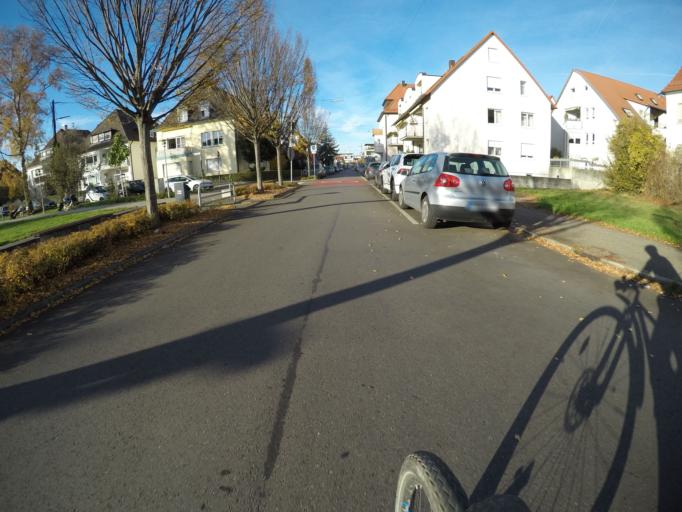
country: DE
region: Baden-Wuerttemberg
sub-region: Regierungsbezirk Stuttgart
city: Fellbach
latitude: 48.8160
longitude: 9.2718
